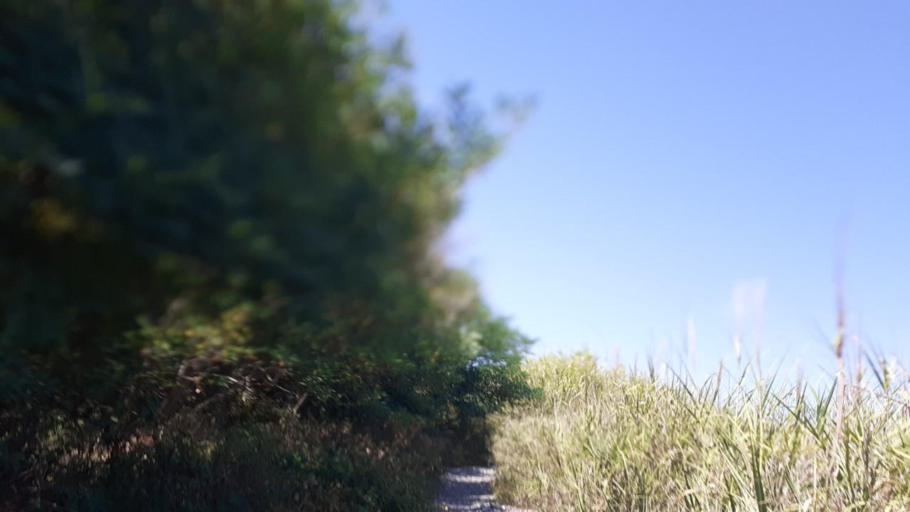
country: IT
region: Abruzzo
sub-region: Provincia di Chieti
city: Torino di Sangro
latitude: 42.2169
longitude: 14.5781
